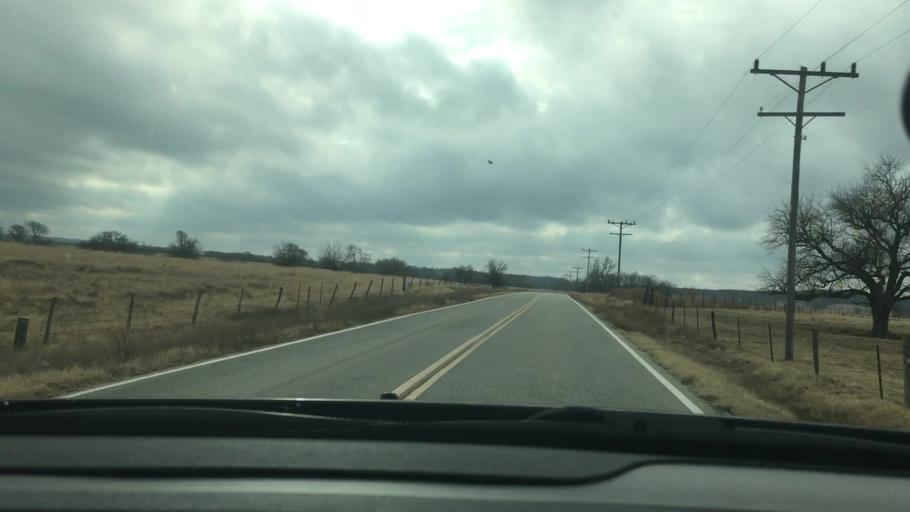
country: US
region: Oklahoma
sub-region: Bryan County
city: Durant
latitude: 34.0919
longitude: -96.4858
